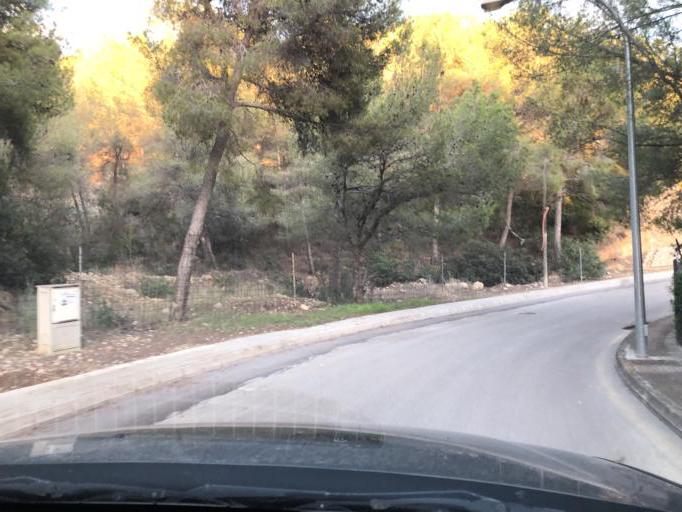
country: ES
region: Balearic Islands
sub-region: Illes Balears
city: Santa Ponsa
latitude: 39.5292
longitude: 2.4691
